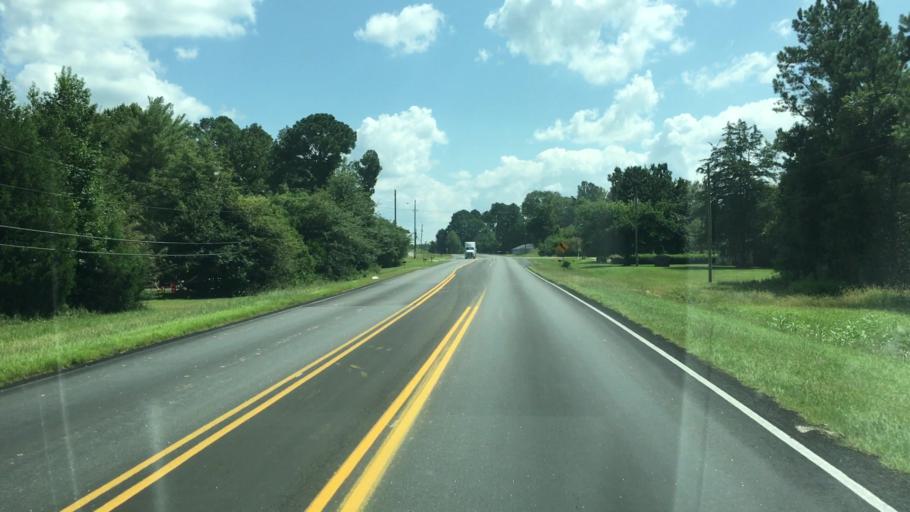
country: US
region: Georgia
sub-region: Morgan County
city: Madison
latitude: 33.6186
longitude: -83.4510
